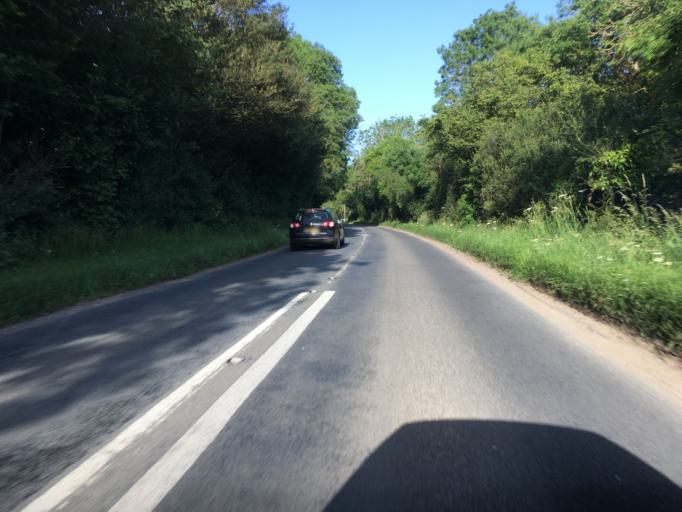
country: GB
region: England
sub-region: Gloucestershire
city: Fairford
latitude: 51.7034
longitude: -1.8066
